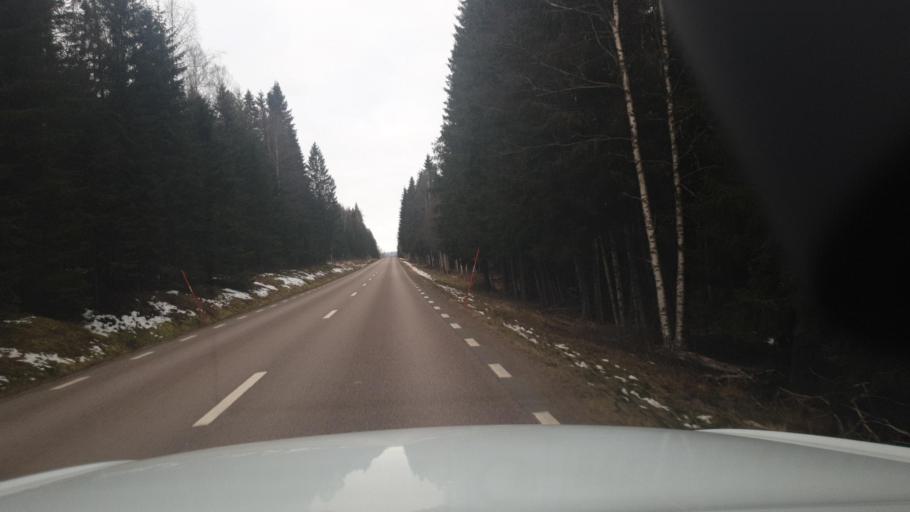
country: SE
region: Vaermland
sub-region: Sunne Kommun
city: Sunne
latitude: 59.8341
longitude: 12.9667
